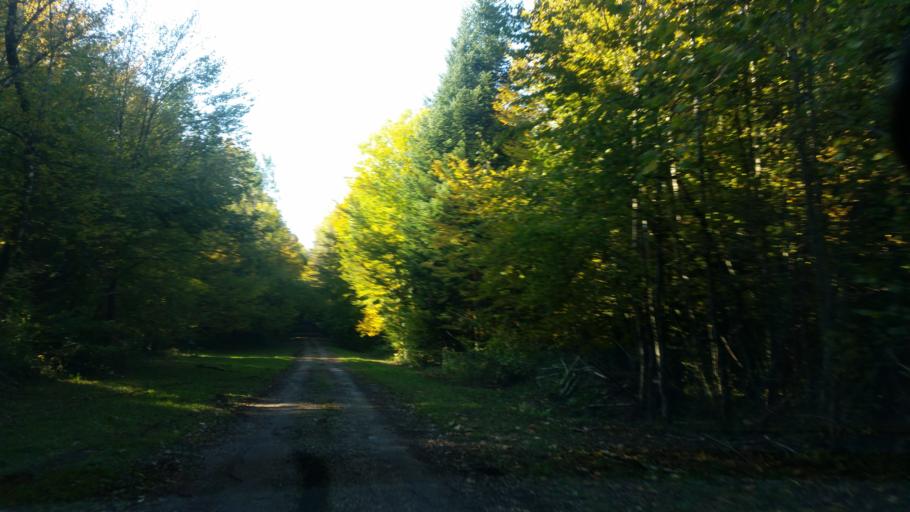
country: FR
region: Franche-Comte
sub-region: Departement du Doubs
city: Levier
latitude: 47.0095
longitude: 6.0017
